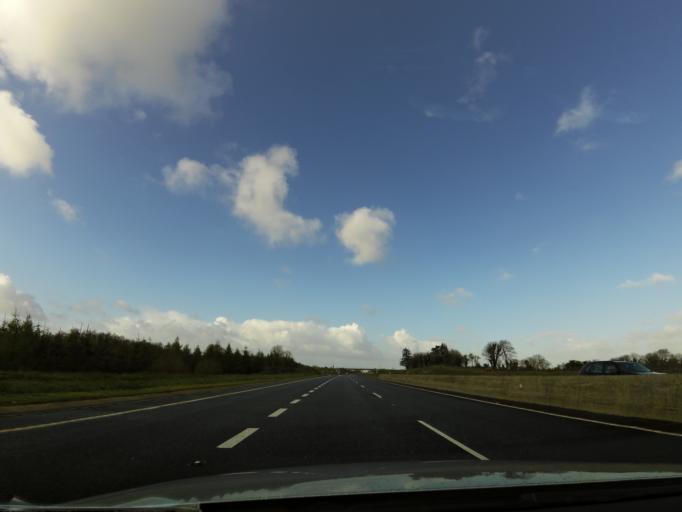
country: IE
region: Munster
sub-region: North Tipperary
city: Newport
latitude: 52.7597
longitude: -8.4020
